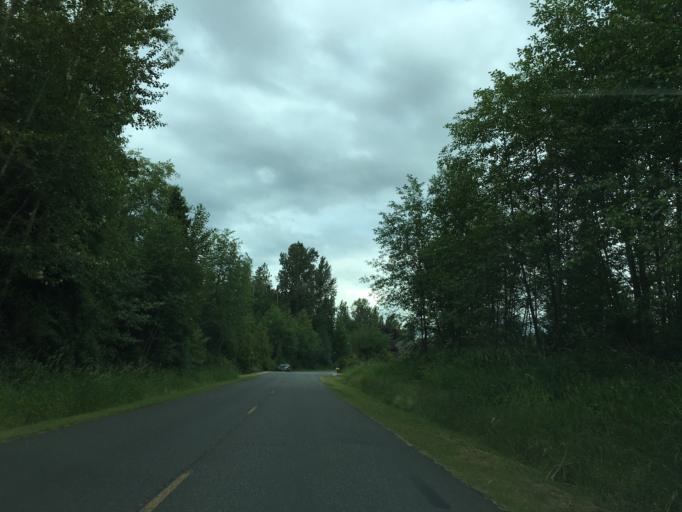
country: US
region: Washington
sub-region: Whatcom County
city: Birch Bay
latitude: 48.9448
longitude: -122.7412
